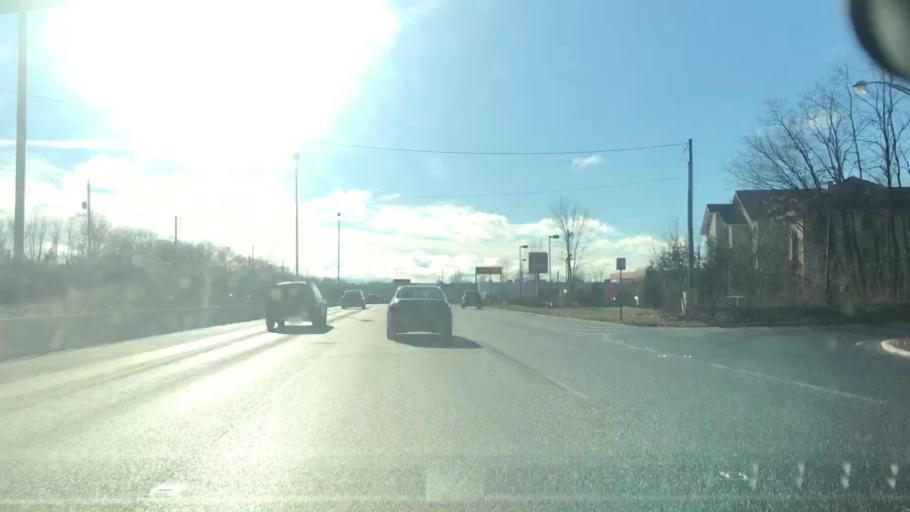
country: US
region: New Jersey
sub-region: Bergen County
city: Mahwah
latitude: 41.0938
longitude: -74.1559
